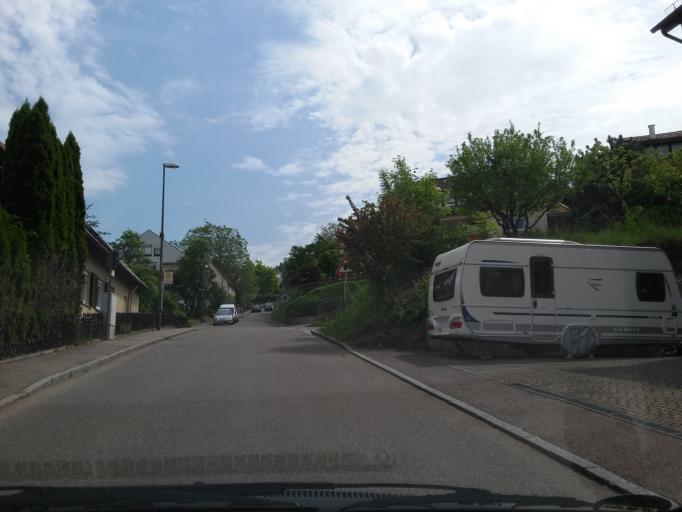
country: DE
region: Baden-Wuerttemberg
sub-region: Regierungsbezirk Stuttgart
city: Esslingen
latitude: 48.7529
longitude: 9.3258
